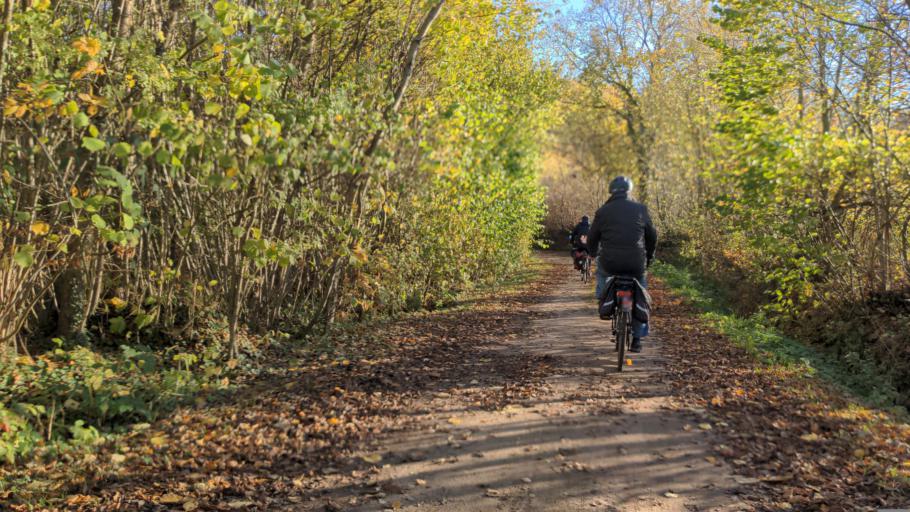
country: DE
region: Schleswig-Holstein
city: Ratekau
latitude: 53.9394
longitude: 10.7709
